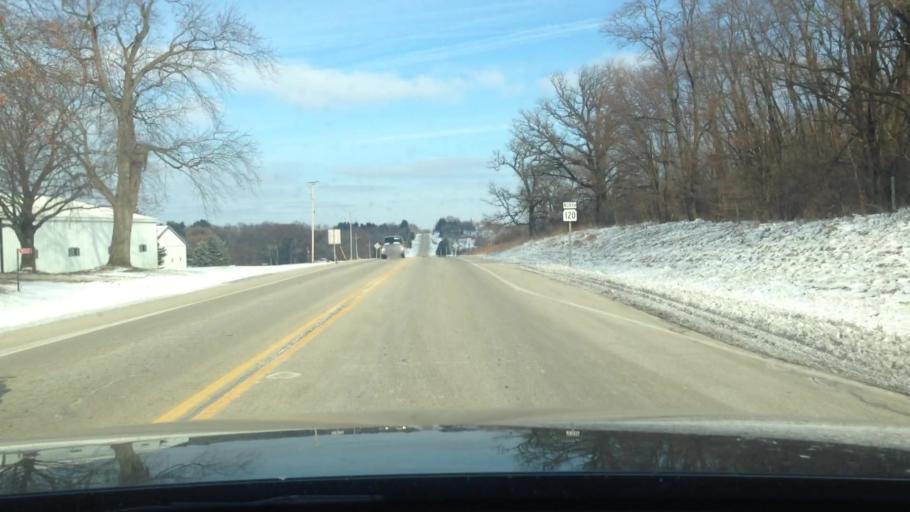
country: US
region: Wisconsin
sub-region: Walworth County
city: East Troy
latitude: 42.7462
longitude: -88.4061
